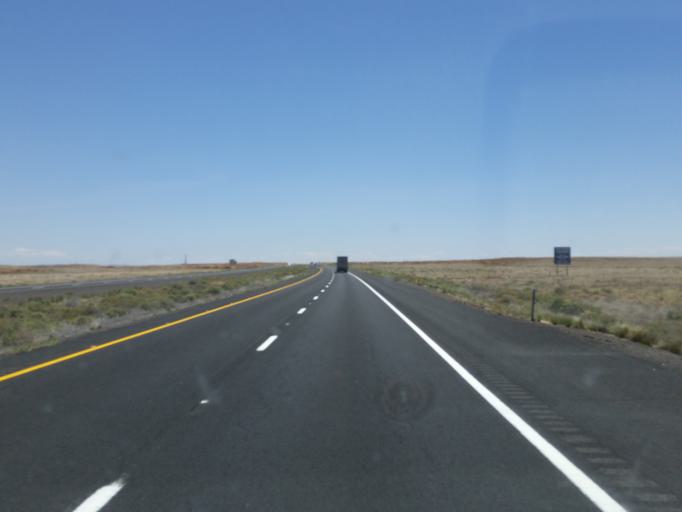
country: US
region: Arizona
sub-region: Coconino County
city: LeChee
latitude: 35.1147
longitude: -111.0734
